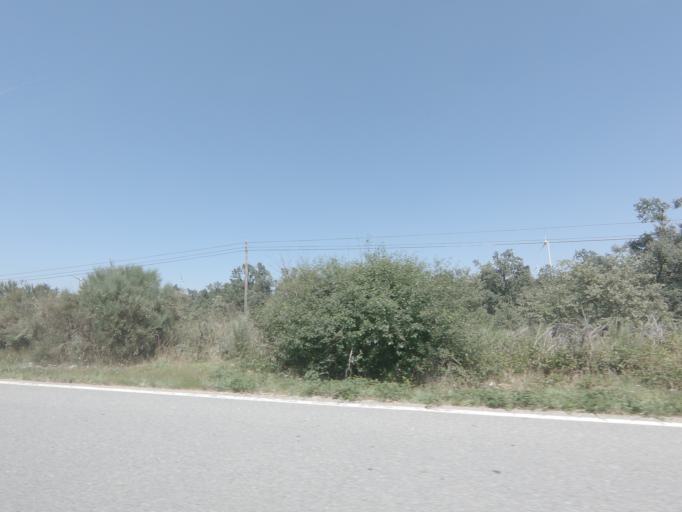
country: PT
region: Viseu
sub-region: Tarouca
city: Tarouca
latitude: 40.9985
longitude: -7.8856
